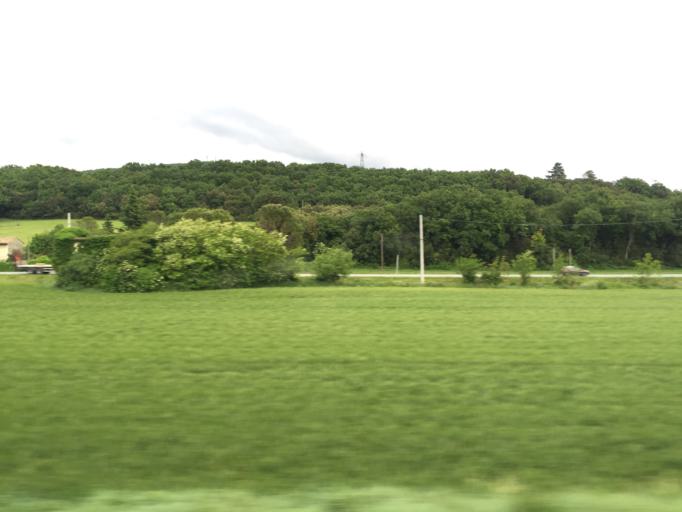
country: FR
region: Rhone-Alpes
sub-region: Departement de la Drome
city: Savasse
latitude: 44.6134
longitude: 4.7554
